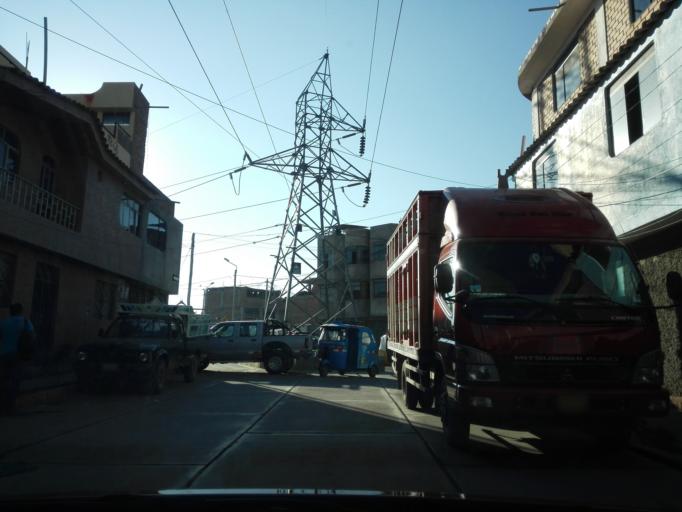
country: PE
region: Ayacucho
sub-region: Provincia de Huamanga
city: Ayacucho
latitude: -13.1507
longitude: -74.2184
